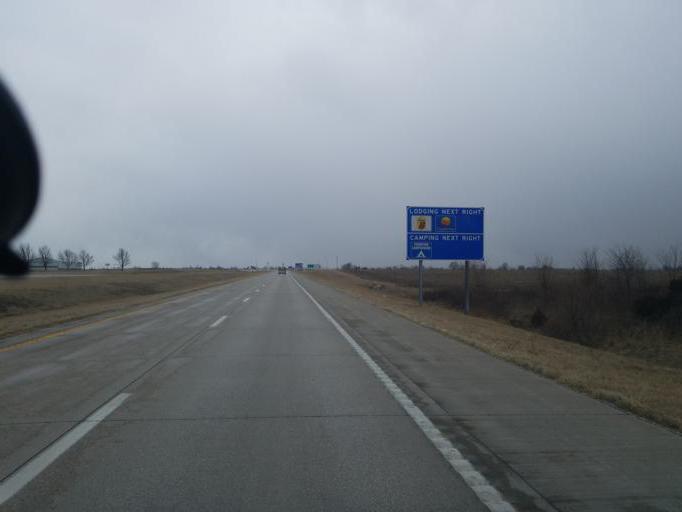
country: US
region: Missouri
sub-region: Randolph County
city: Moberly
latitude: 39.4673
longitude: -92.4351
